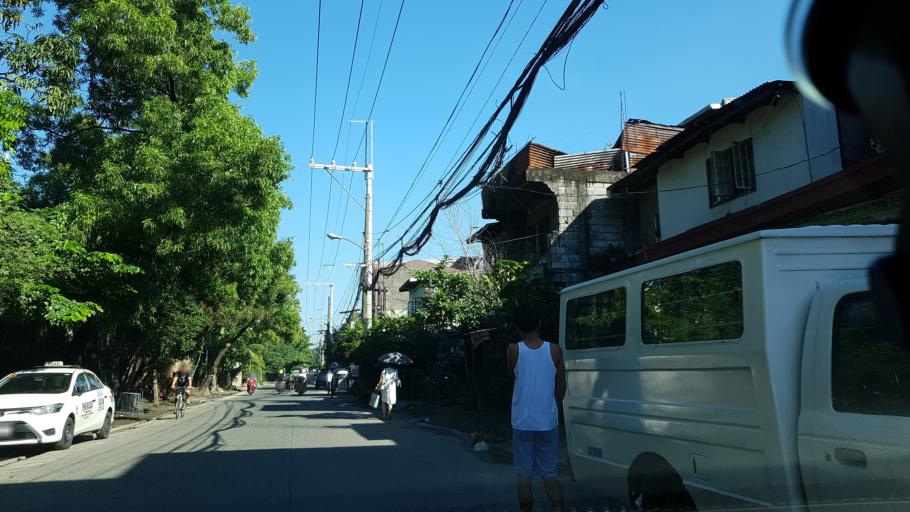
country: PH
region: Calabarzon
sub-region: Province of Rizal
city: Cainta
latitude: 14.5733
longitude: 121.1001
